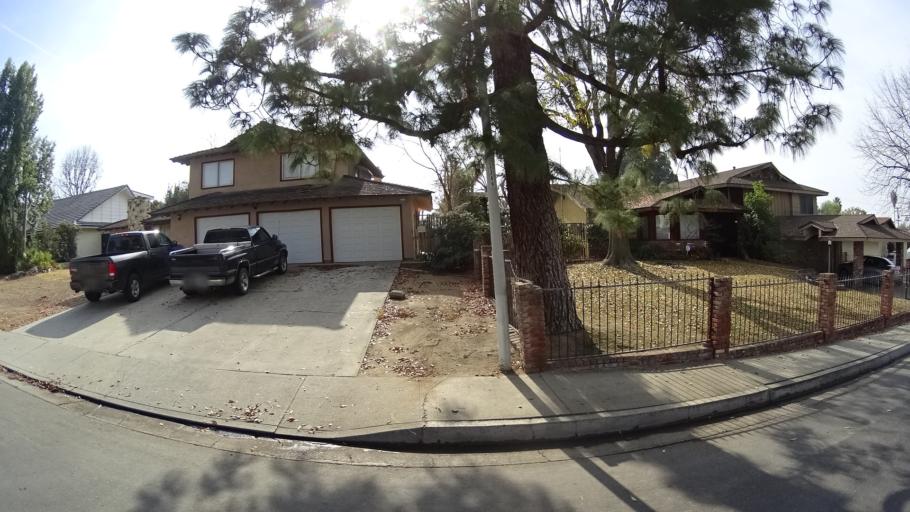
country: US
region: California
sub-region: Kern County
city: Oildale
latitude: 35.4123
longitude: -118.9598
